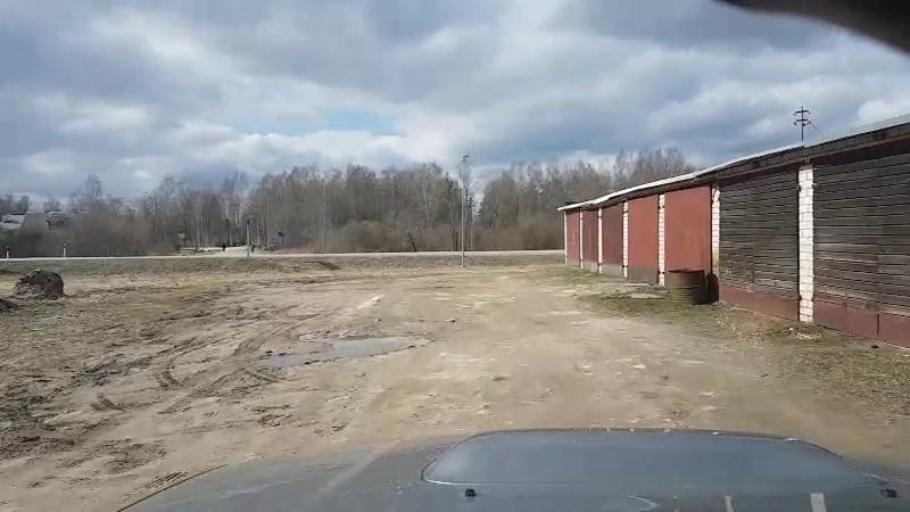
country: EE
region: Jaervamaa
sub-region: Paide linn
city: Paide
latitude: 58.8829
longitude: 25.5341
